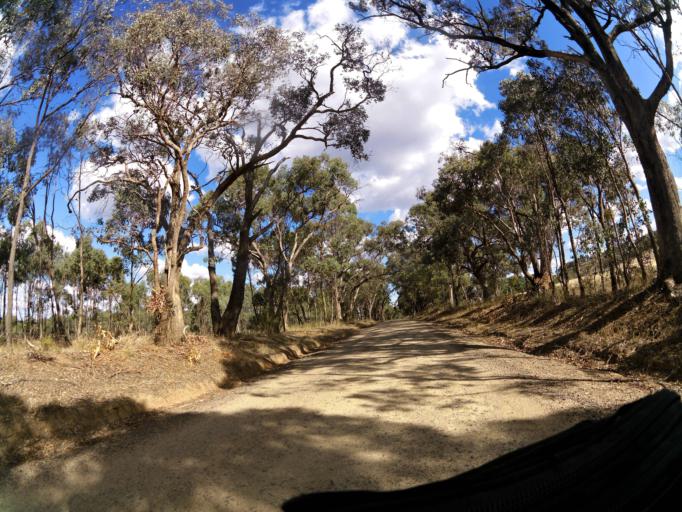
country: AU
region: Victoria
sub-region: Greater Bendigo
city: Kennington
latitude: -36.9963
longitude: 144.8127
